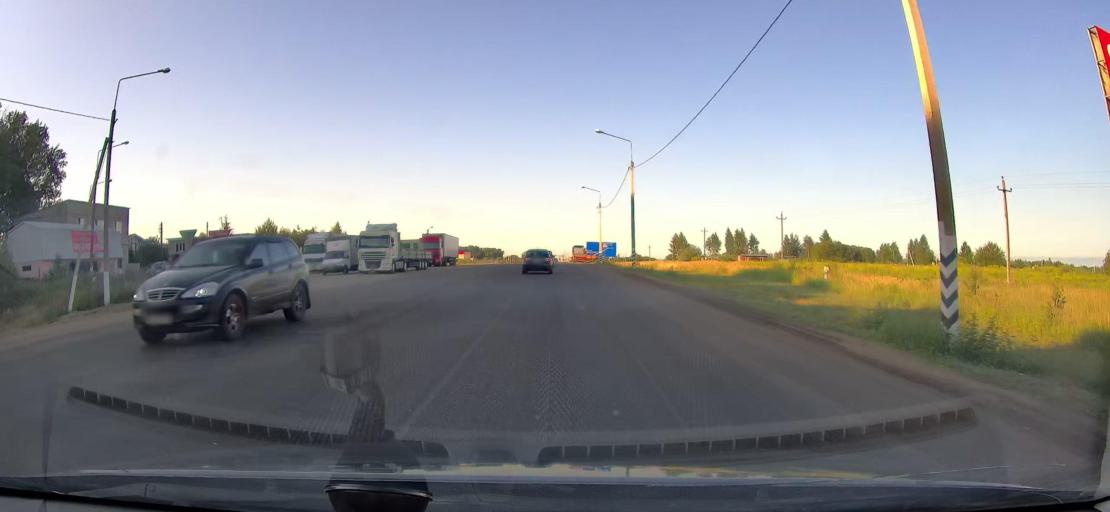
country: RU
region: Tula
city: Shchekino
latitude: 54.0021
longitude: 37.4753
